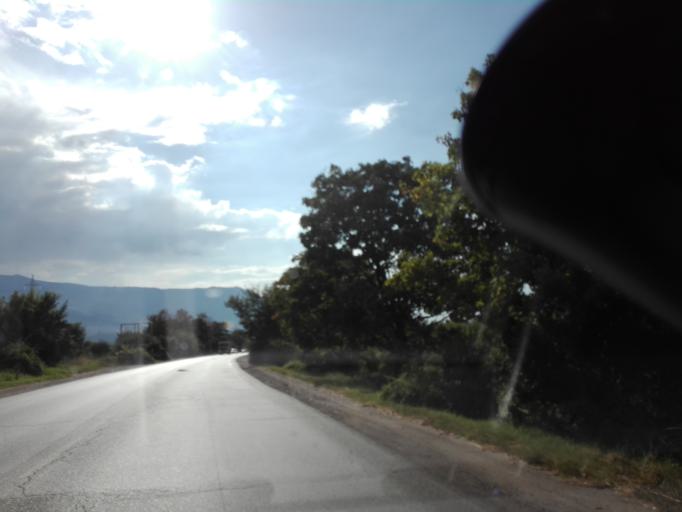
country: BG
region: Sofia-Capital
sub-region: Stolichna Obshtina
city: Sofia
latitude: 42.6215
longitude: 23.4366
